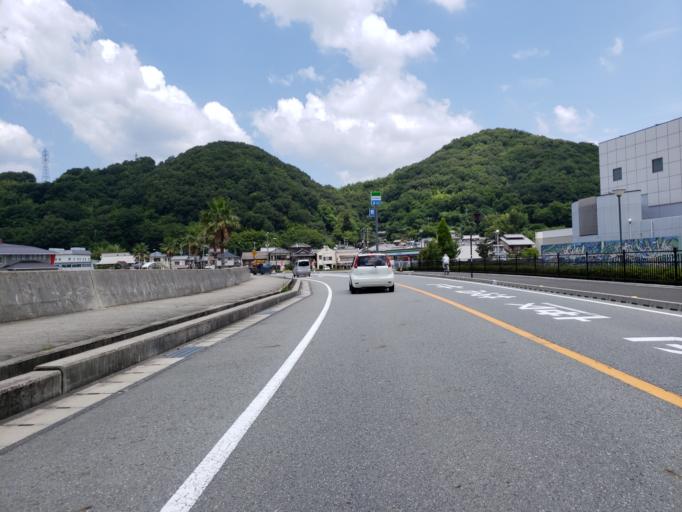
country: JP
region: Hyogo
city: Aioi
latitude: 34.7969
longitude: 134.4702
